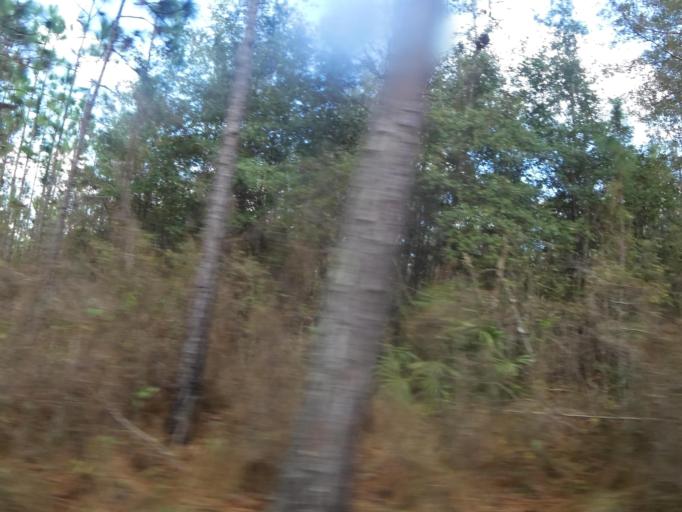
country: US
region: Florida
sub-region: Clay County
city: Middleburg
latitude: 30.1474
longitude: -81.9590
